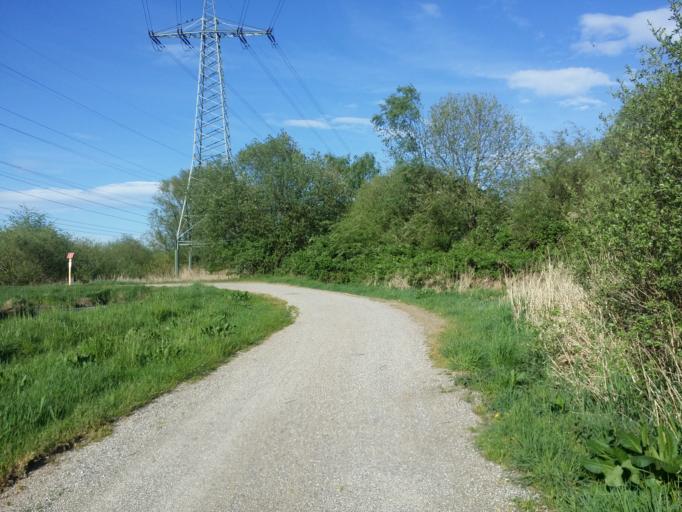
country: DE
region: Lower Saxony
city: Lemwerder
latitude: 53.1393
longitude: 8.6584
